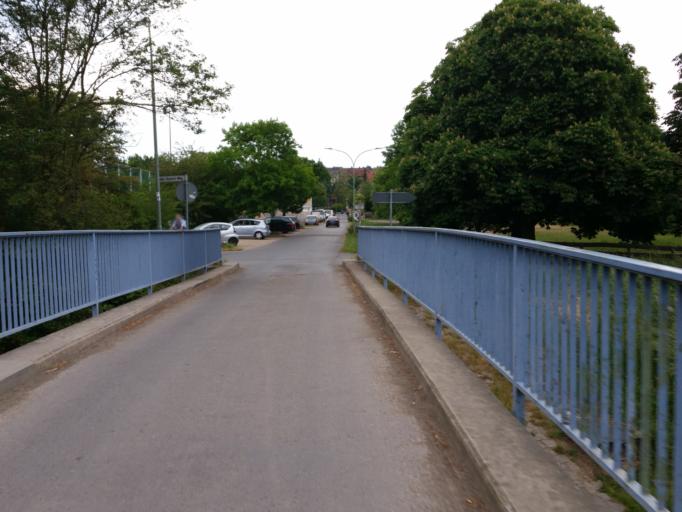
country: DE
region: Hesse
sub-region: Regierungsbezirk Darmstadt
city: Karben
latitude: 50.2235
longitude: 8.7687
